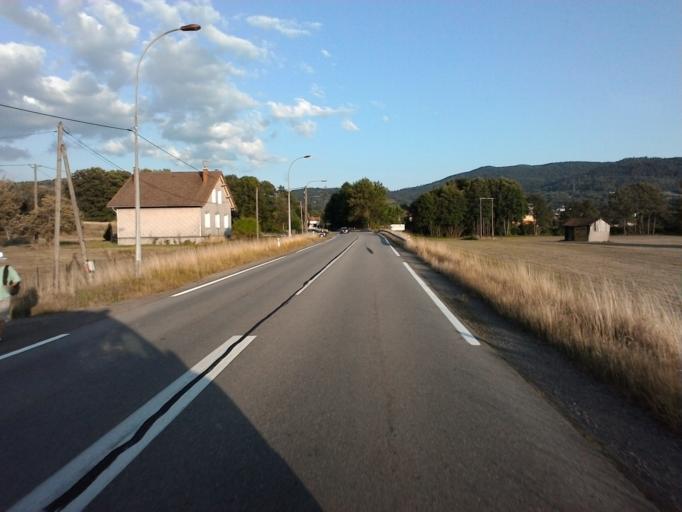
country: FR
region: Lorraine
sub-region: Departement des Vosges
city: Ramonchamp
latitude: 47.8885
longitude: 6.7504
